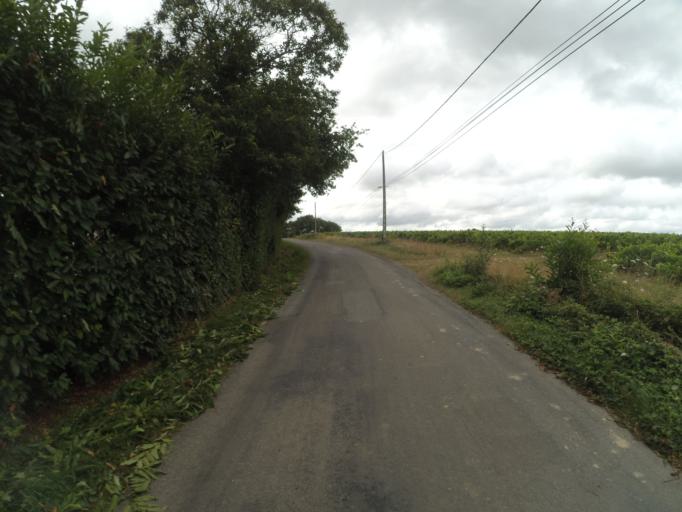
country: FR
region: Pays de la Loire
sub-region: Departement de la Vendee
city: Saint-Philbert-de-Bouaine
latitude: 47.0080
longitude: -1.5380
